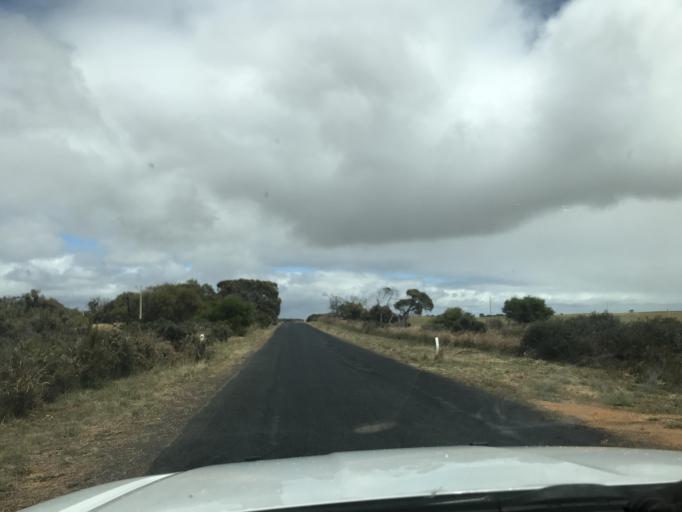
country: AU
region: South Australia
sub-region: Tatiara
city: Bordertown
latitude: -36.1356
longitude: 141.1867
